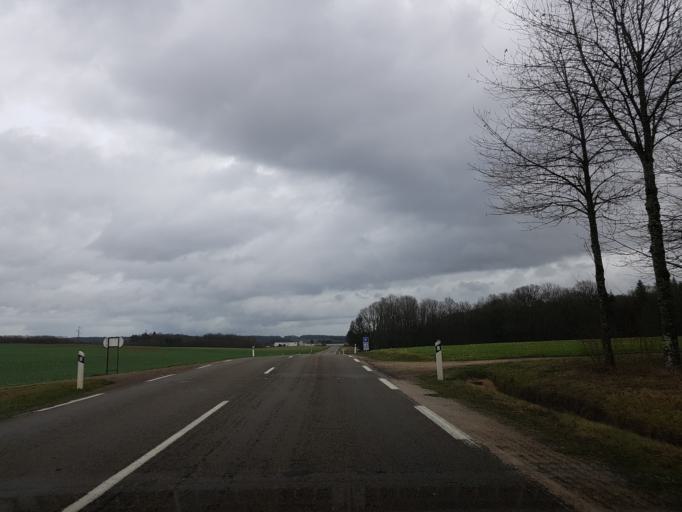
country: FR
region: Franche-Comte
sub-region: Departement de la Haute-Saone
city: Jussey
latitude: 47.7189
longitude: 5.8701
